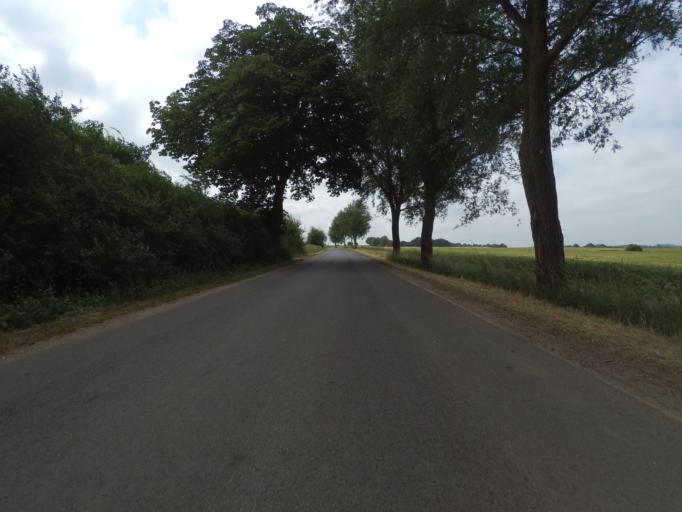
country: DE
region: Mecklenburg-Vorpommern
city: Malchow
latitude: 53.4762
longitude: 12.4629
